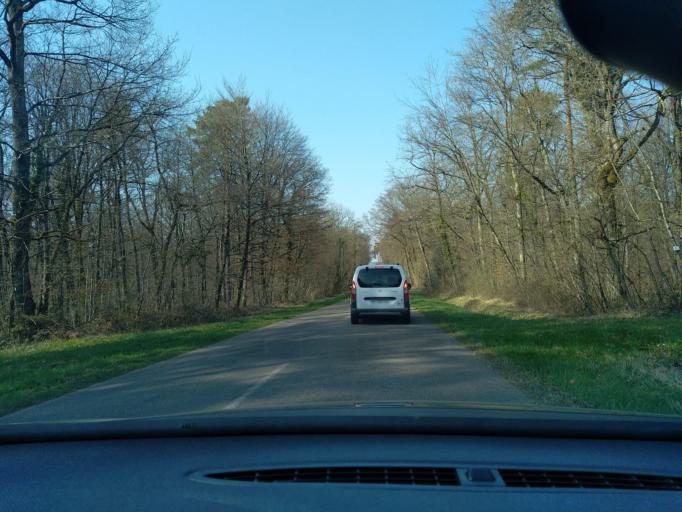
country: FR
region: Franche-Comte
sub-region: Departement du Jura
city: Dole
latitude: 47.0661
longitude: 5.5071
